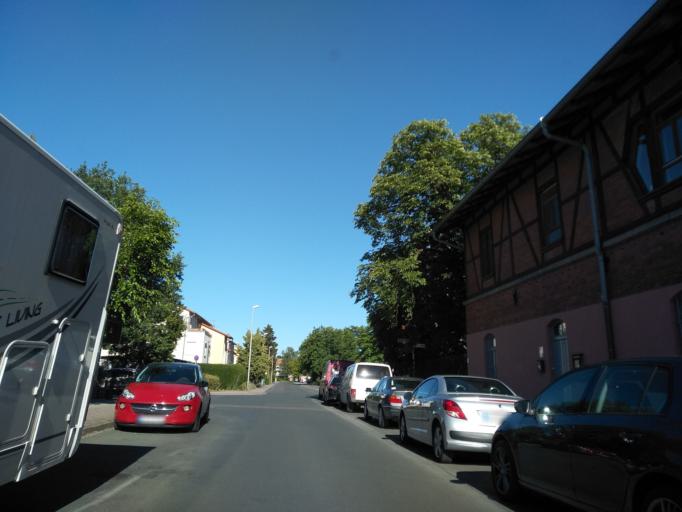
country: DE
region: Bavaria
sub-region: Regierungsbezirk Mittelfranken
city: Erlangen
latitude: 49.5982
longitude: 11.0257
